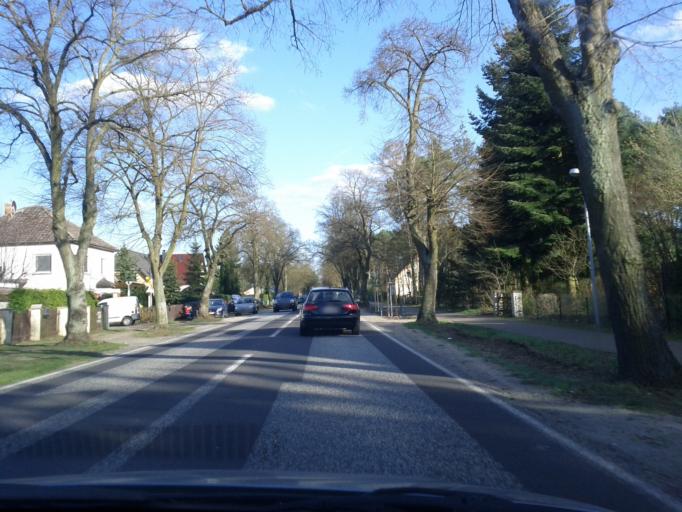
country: DE
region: Brandenburg
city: Spreenhagen
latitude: 52.3917
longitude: 13.9427
